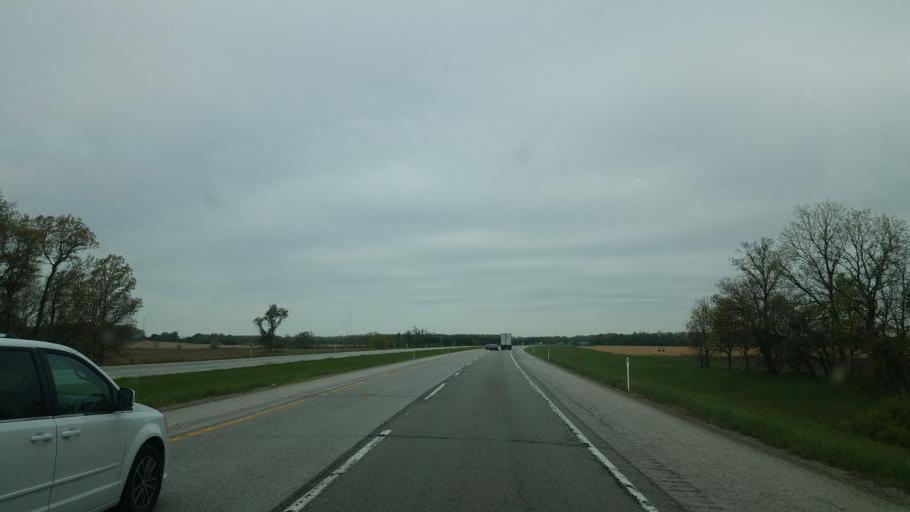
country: US
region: Michigan
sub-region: Saint Joseph County
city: White Pigeon
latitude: 41.7517
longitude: -85.6249
